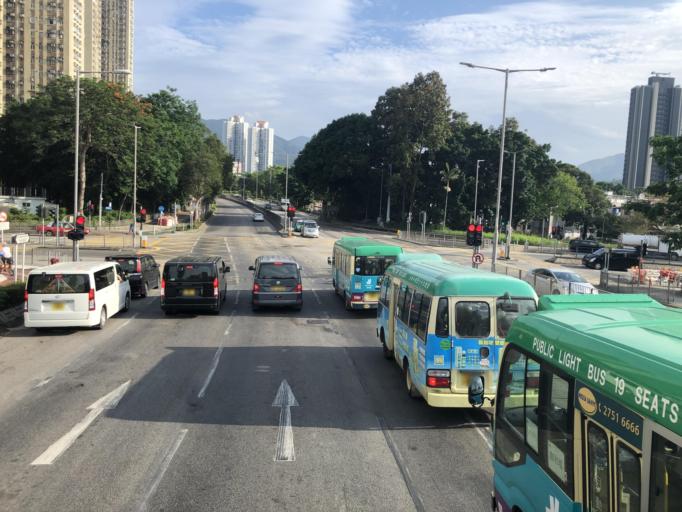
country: CN
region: Guangdong
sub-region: Shenzhen
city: Shenzhen
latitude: 22.5037
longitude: 114.1236
